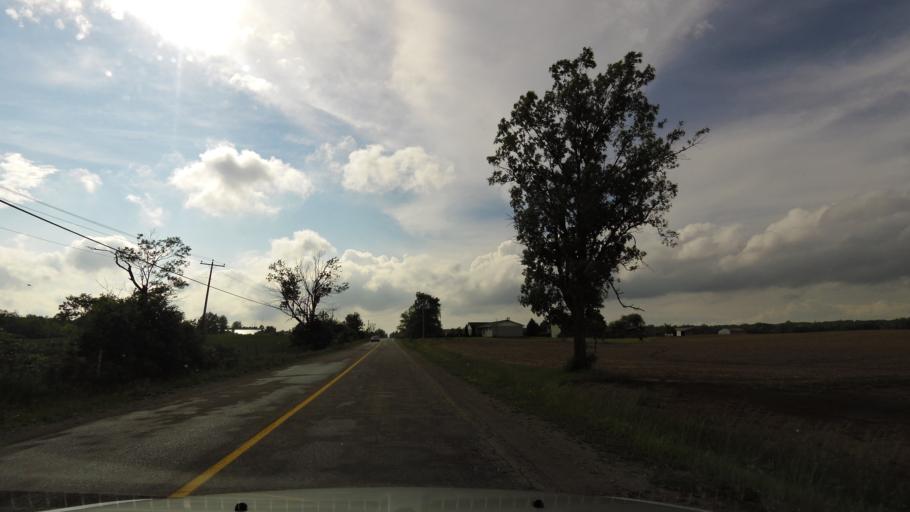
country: CA
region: Ontario
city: Ancaster
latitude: 43.0177
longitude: -80.0357
